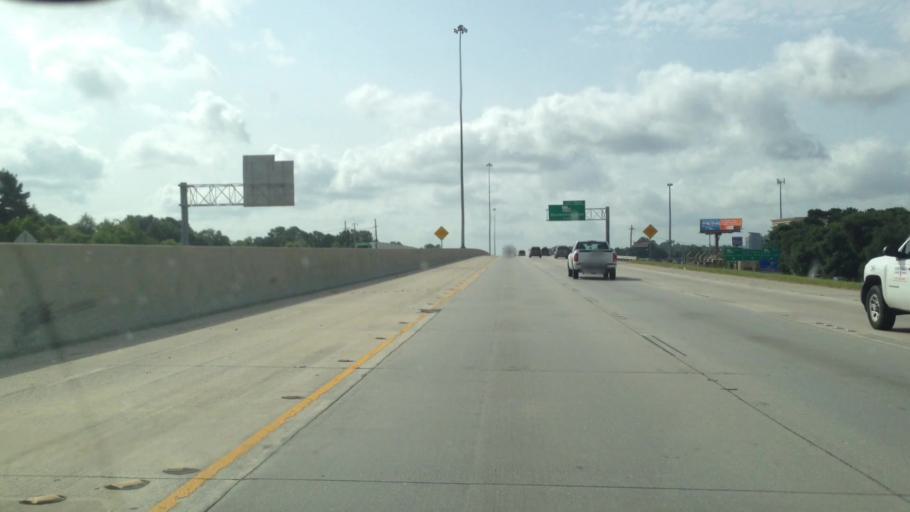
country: US
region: Louisiana
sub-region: East Baton Rouge Parish
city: Westminster
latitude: 30.4096
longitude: -91.1041
